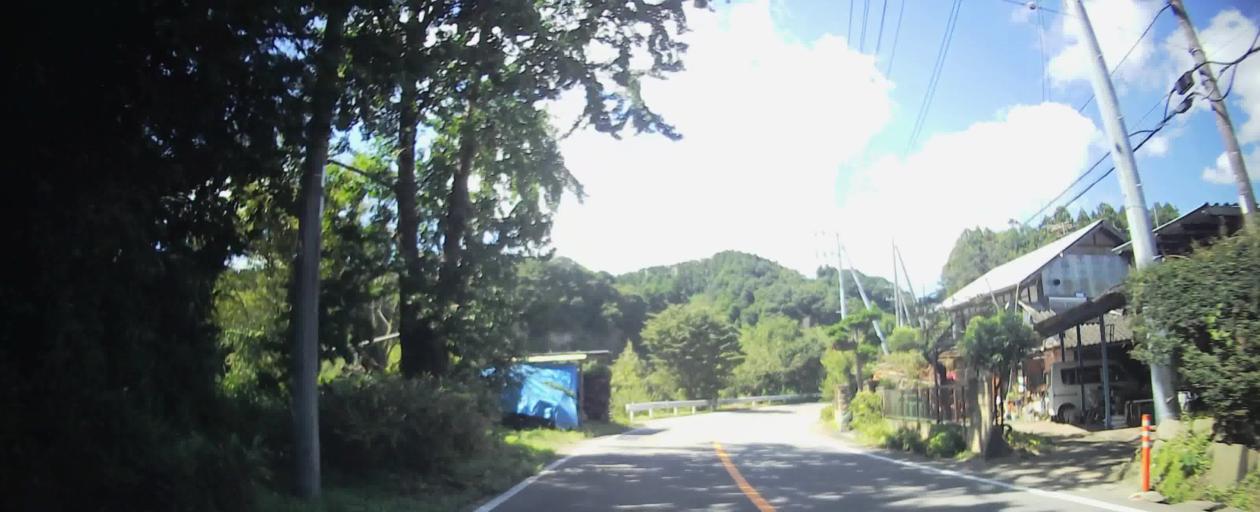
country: JP
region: Gunma
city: Kanekomachi
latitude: 36.4190
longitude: 138.9396
